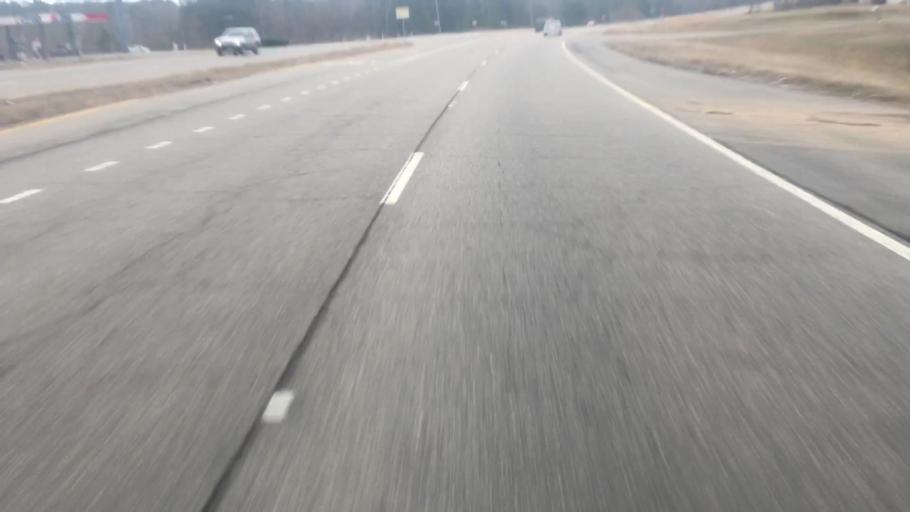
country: US
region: Alabama
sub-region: Walker County
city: Cordova
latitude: 33.8204
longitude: -87.1542
